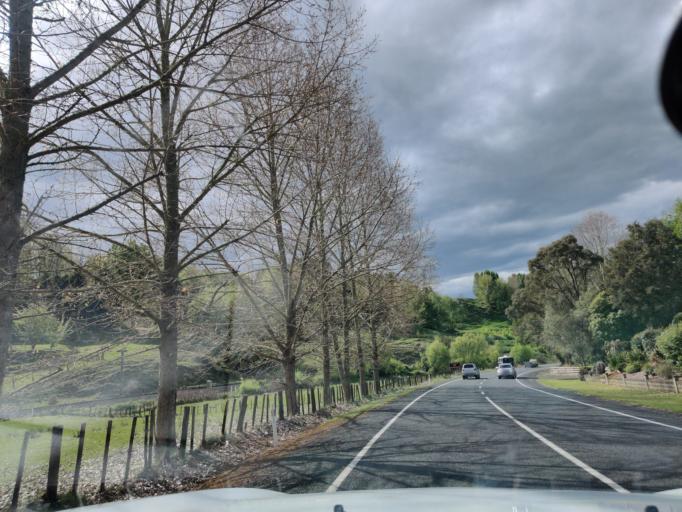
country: NZ
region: Waikato
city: Turangi
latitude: -38.9197
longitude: 175.3360
